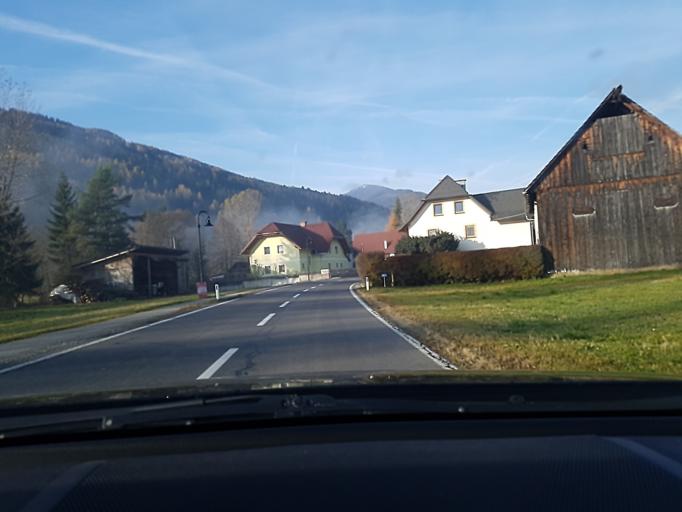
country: AT
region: Styria
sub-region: Politischer Bezirk Murau
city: Ranten
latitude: 47.1568
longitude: 14.0862
